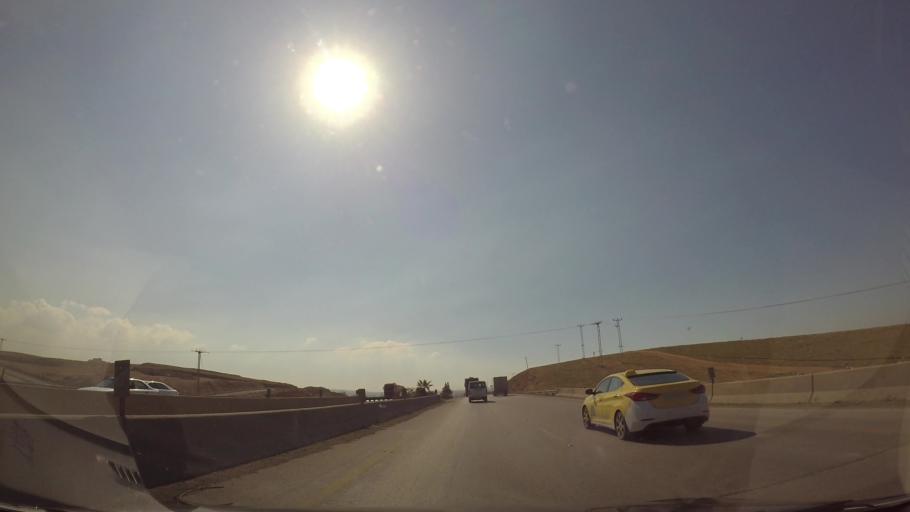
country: JO
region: Zarqa
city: Zarqa
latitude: 32.0443
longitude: 36.1134
